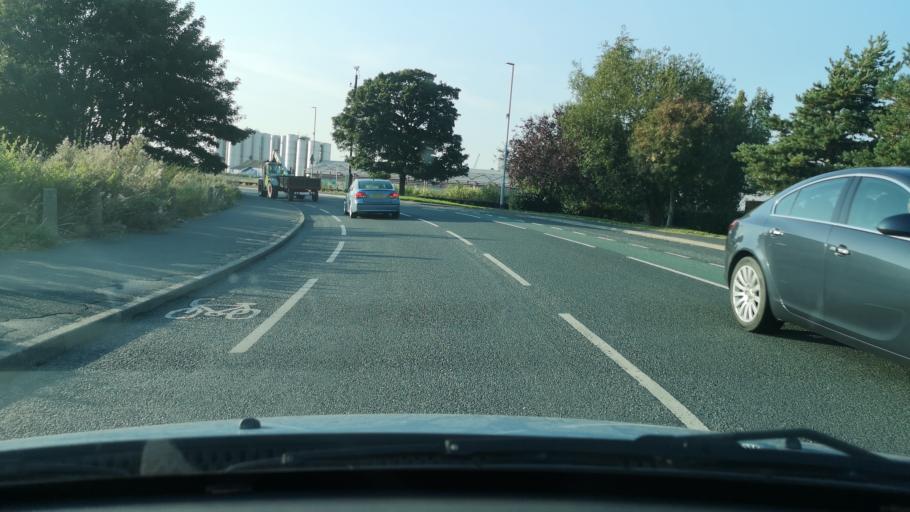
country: GB
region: England
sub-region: East Riding of Yorkshire
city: Goole
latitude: 53.6958
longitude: -0.8698
